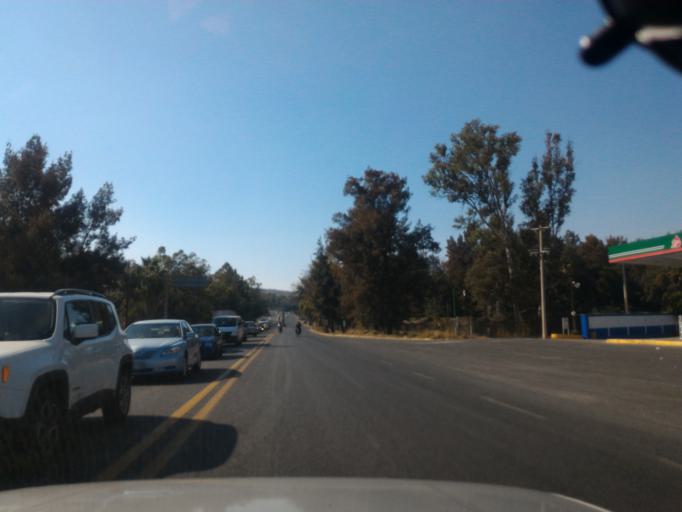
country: MX
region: Jalisco
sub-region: Poncitlan
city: Cuitzeo (La Estancia)
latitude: 20.3473
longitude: -102.7840
